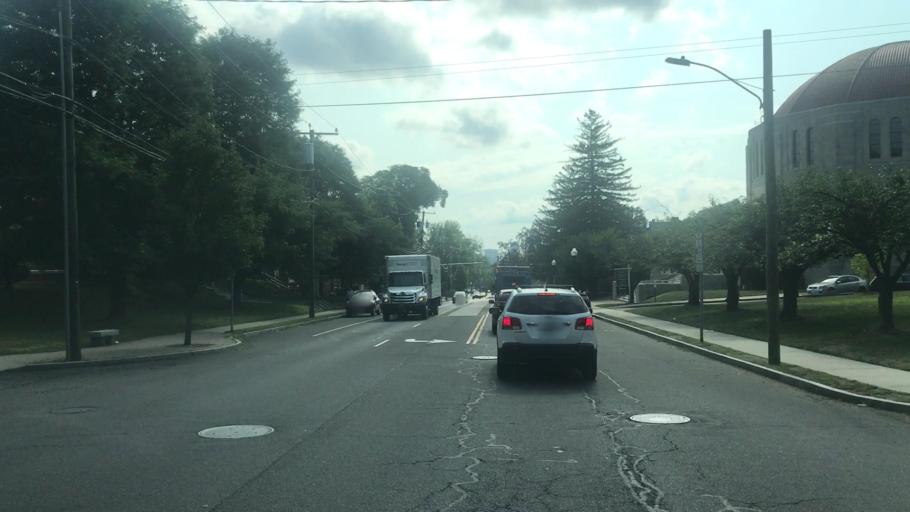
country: US
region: Connecticut
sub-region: Hartford County
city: West Hartford
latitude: 41.7653
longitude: -72.7203
